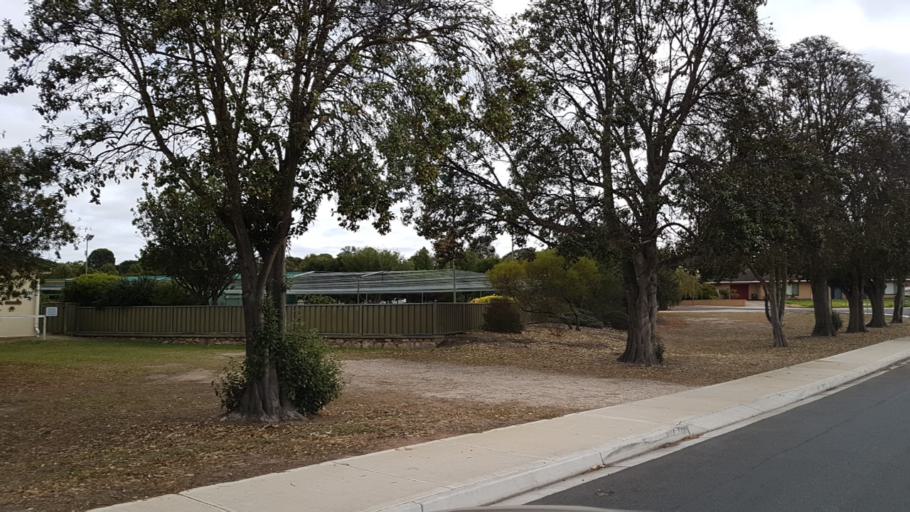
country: AU
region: South Australia
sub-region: Alexandrina
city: Langhorne Creek
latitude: -35.4088
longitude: 138.9714
